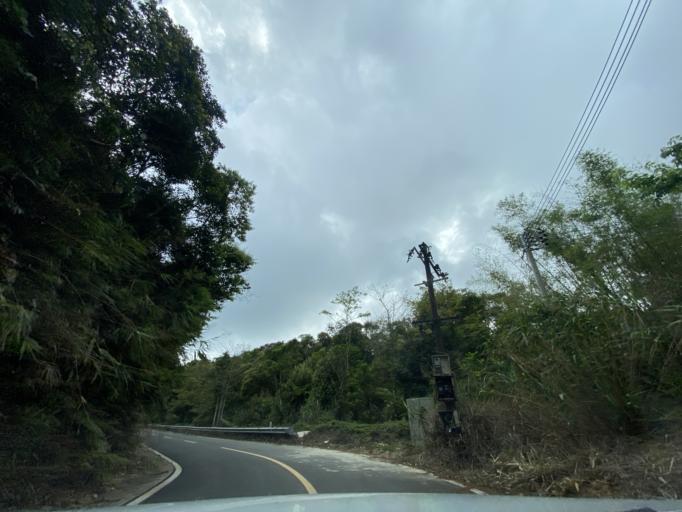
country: CN
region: Hainan
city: Diaoluoshan
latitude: 18.7231
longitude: 109.8697
